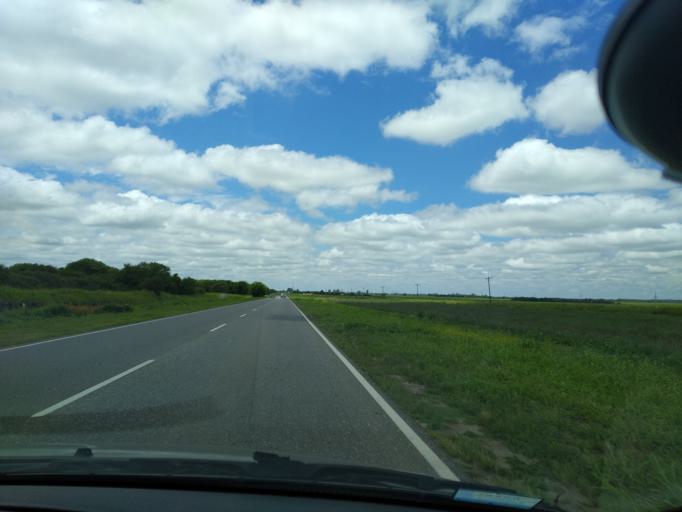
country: AR
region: Cordoba
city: Toledo
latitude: -31.6489
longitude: -64.1206
